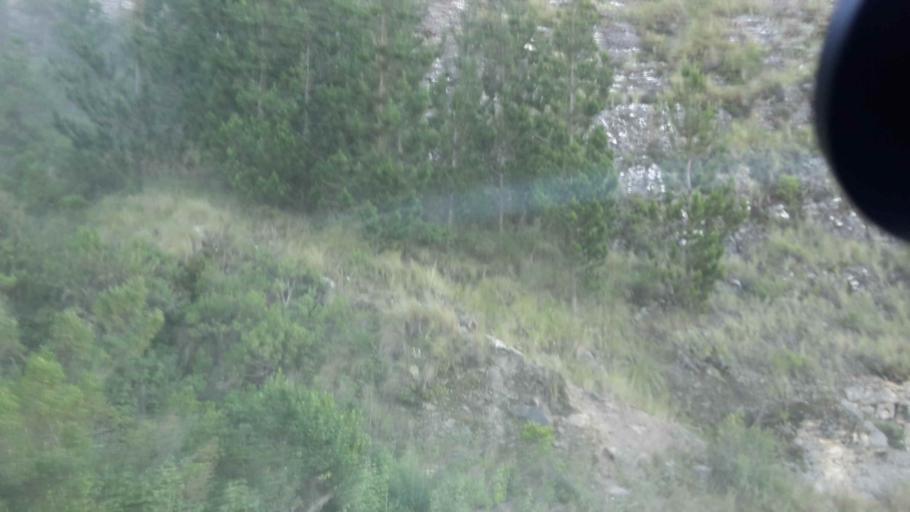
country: BO
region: Cochabamba
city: Arani
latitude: -17.7228
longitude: -65.6409
